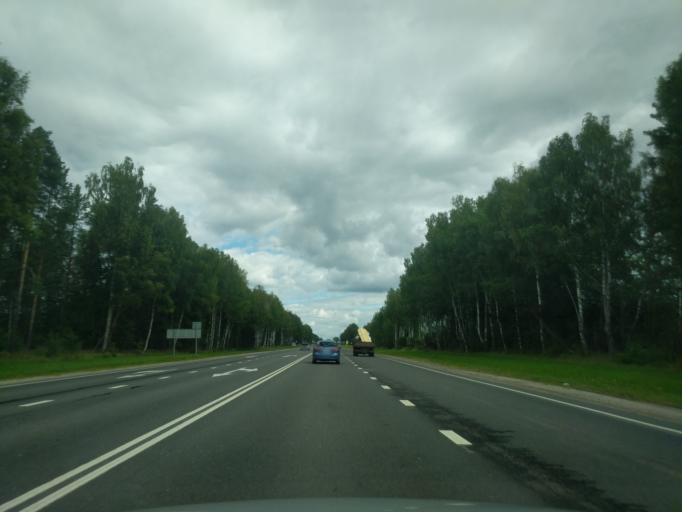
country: RU
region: Jaroslavl
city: Nekrasovskoye
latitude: 57.6054
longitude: 40.3261
